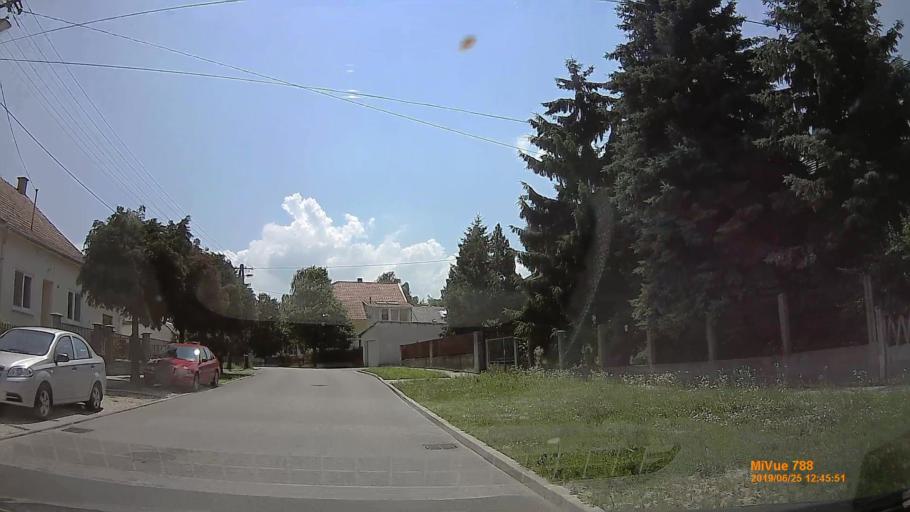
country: HU
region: Komarom-Esztergom
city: Esztergom
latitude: 47.8062
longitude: 18.7462
